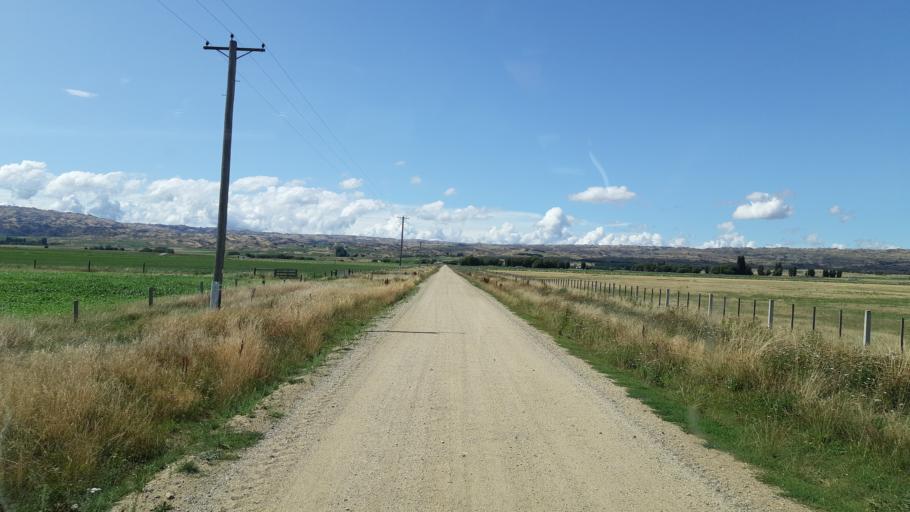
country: NZ
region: Otago
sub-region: Queenstown-Lakes District
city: Wanaka
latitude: -45.2083
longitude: 169.6669
